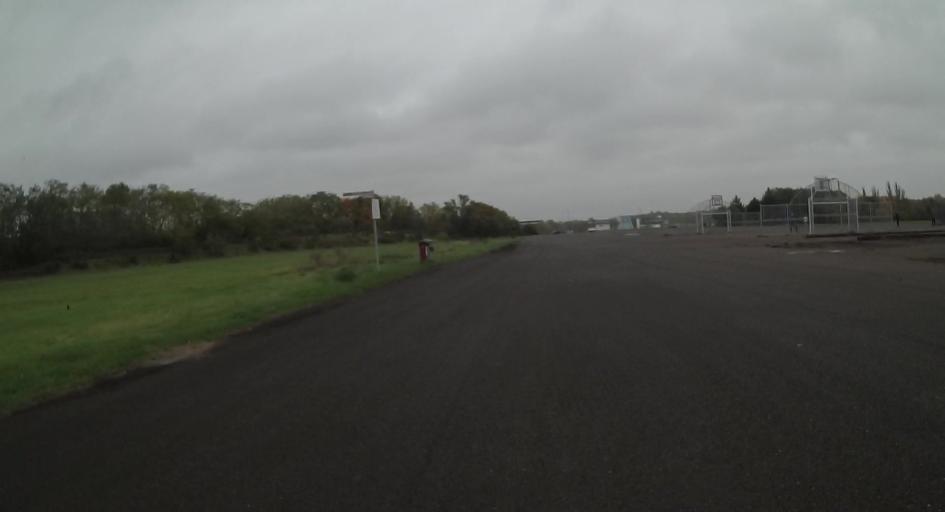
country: GB
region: England
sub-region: Surrey
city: Byfleet
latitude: 51.3457
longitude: -0.4721
